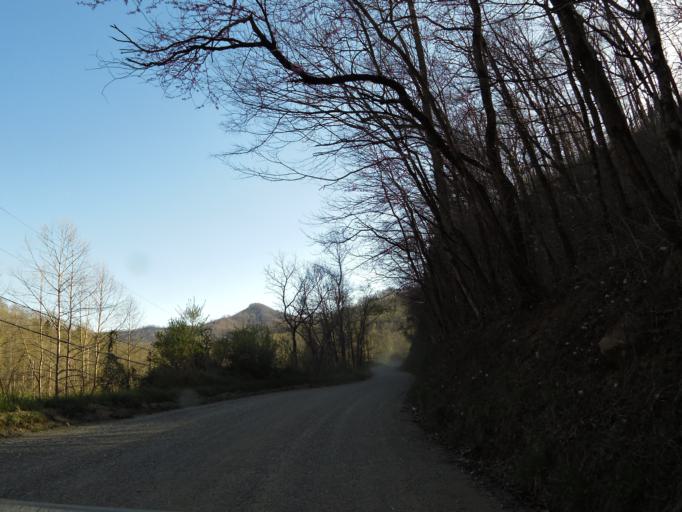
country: US
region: Tennessee
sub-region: Campbell County
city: Caryville
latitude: 36.2627
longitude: -84.3929
